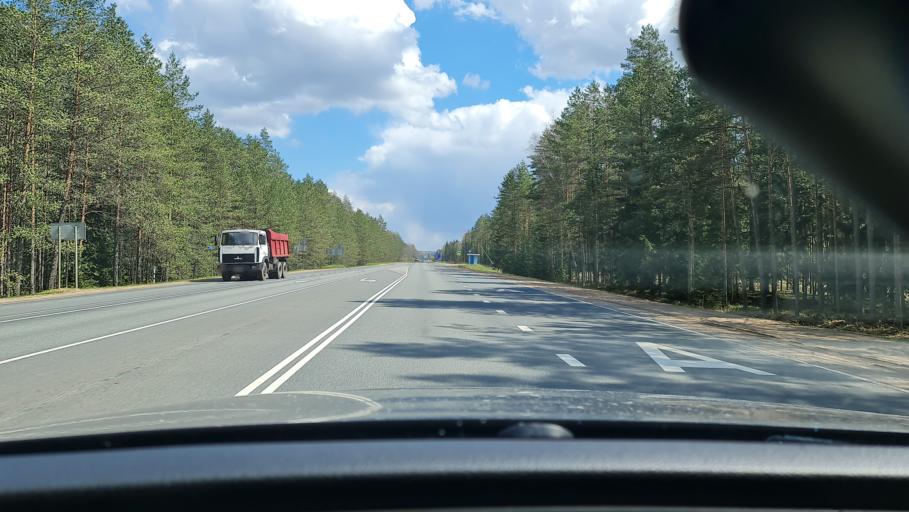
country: RU
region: Tverskaya
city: Zapadnaya Dvina
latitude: 56.3054
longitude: 32.1829
